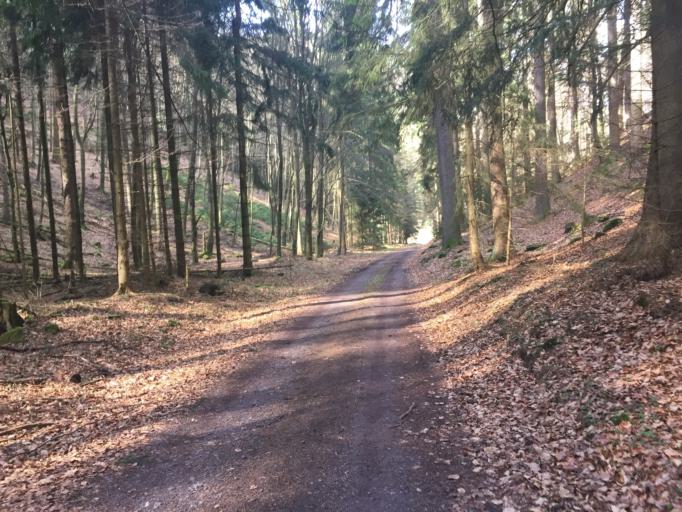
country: DE
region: Rheinland-Pfalz
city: Ramberg
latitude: 49.3037
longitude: 8.0270
